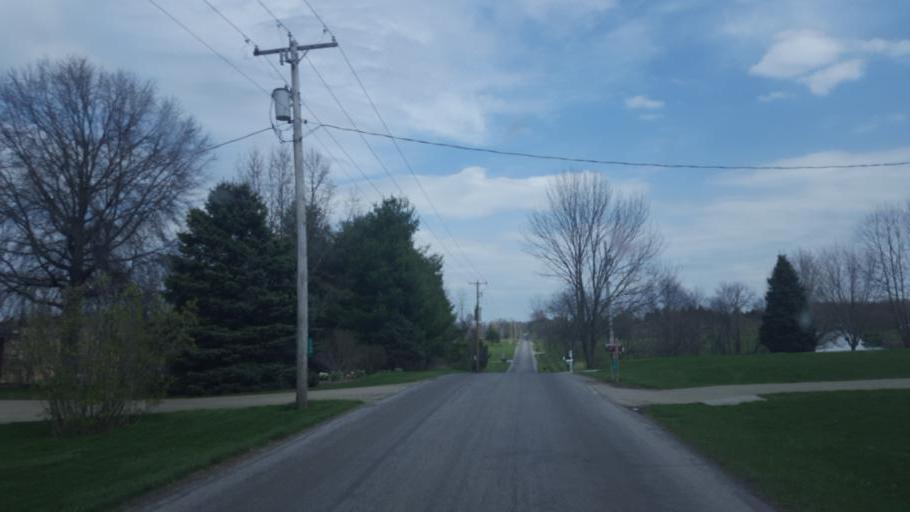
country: US
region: Ohio
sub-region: Sandusky County
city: Bellville
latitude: 40.5864
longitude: -82.5861
